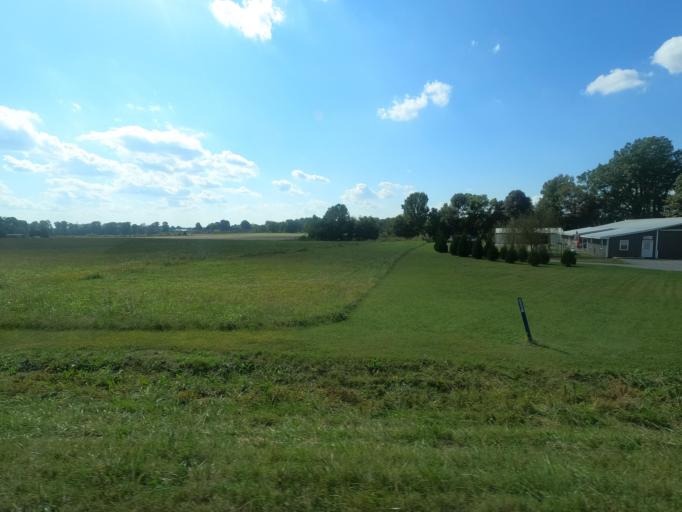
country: US
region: Illinois
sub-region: Massac County
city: Metropolis
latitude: 37.2239
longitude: -88.7322
